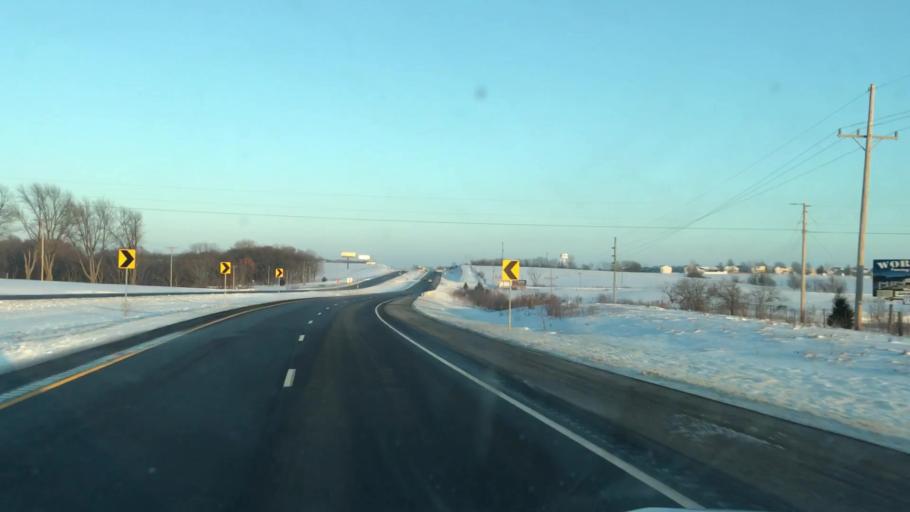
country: US
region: Missouri
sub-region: Clinton County
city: Cameron
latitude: 39.7539
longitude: -94.2680
